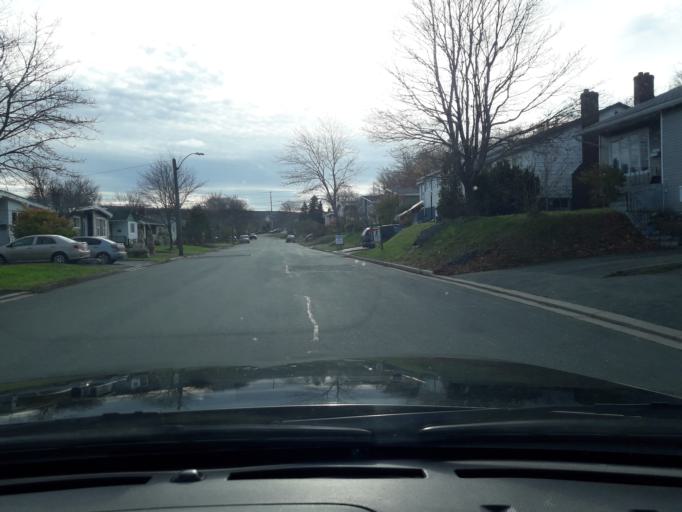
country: CA
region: Newfoundland and Labrador
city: St. John's
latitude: 47.5670
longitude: -52.7504
